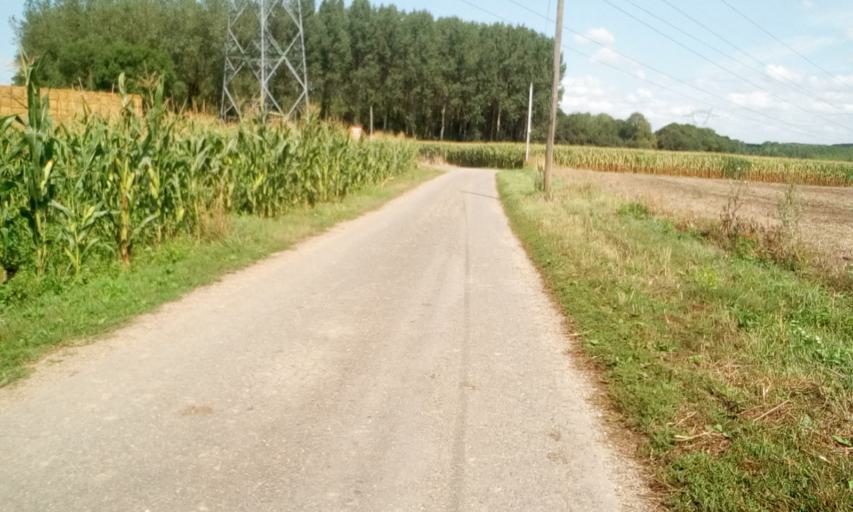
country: FR
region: Lower Normandy
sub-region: Departement du Calvados
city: Argences
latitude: 49.1330
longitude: -0.1872
